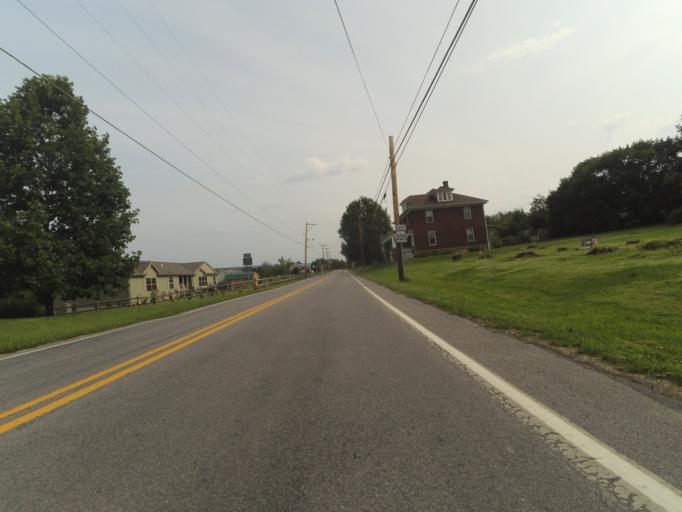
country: US
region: Pennsylvania
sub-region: Huntingdon County
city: Huntingdon
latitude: 40.5759
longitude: -78.0476
